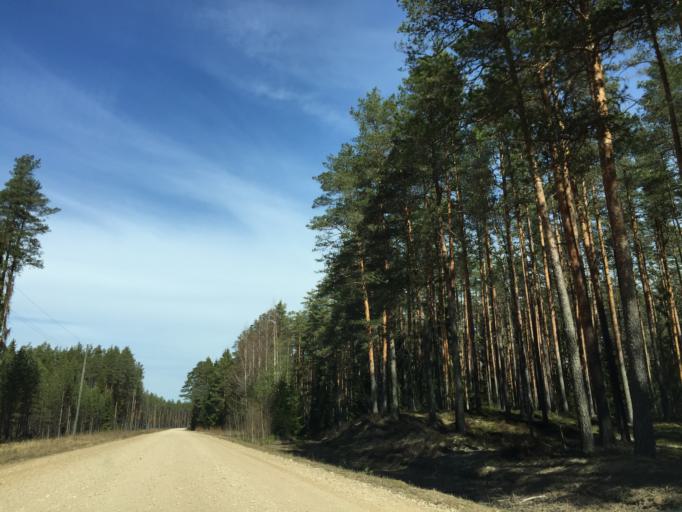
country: LV
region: Strenci
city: Seda
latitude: 57.6348
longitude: 25.8603
